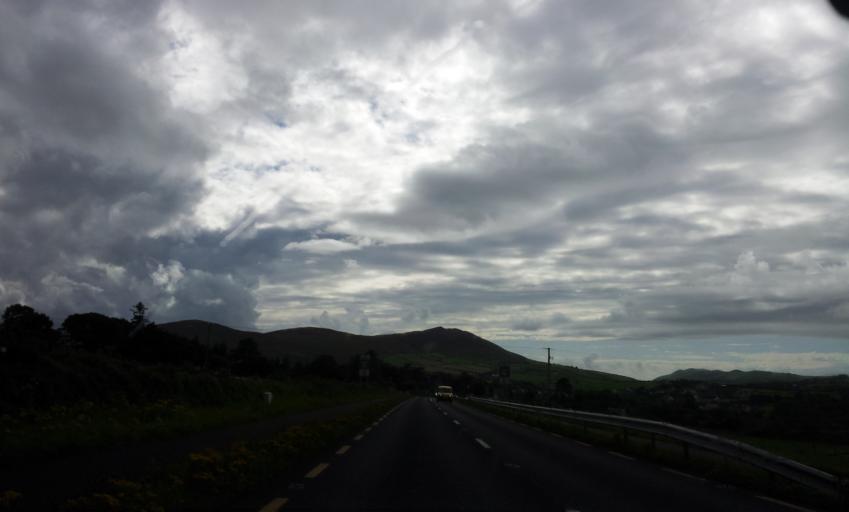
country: IE
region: Munster
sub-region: Ciarrai
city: Dingle
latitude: 52.1568
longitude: -10.0416
